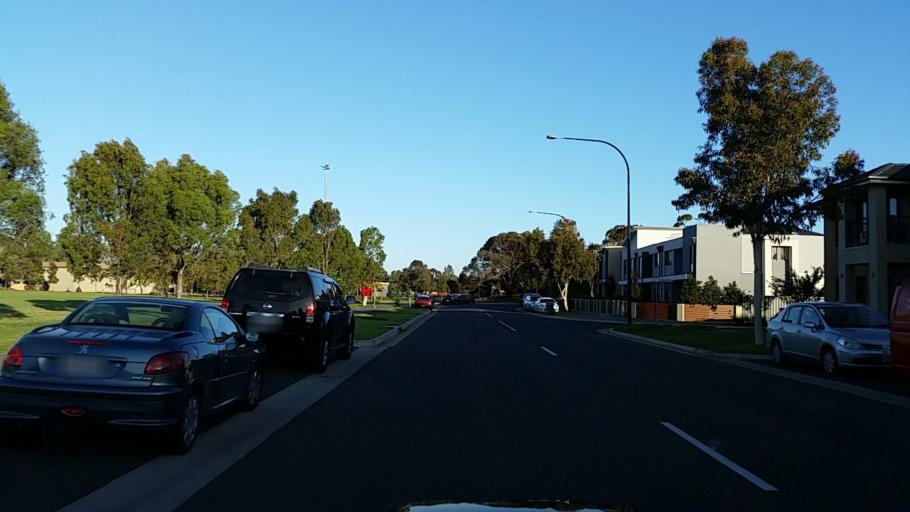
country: AU
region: South Australia
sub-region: Charles Sturt
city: Woodville North
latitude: -34.8738
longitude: 138.5359
